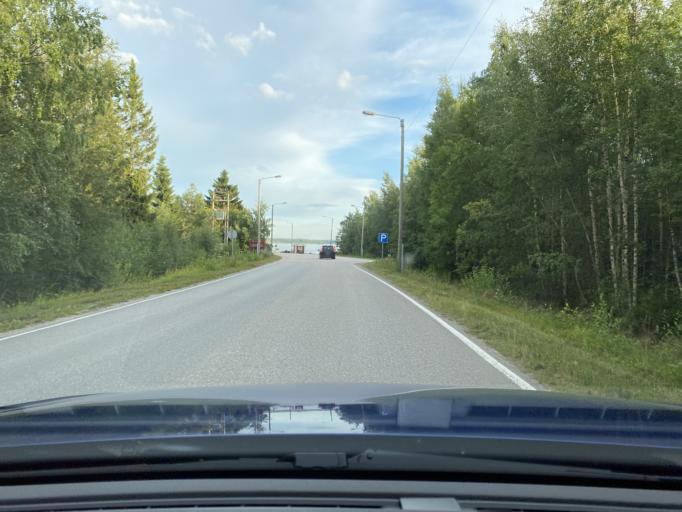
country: FI
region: Ostrobothnia
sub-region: Vaasa
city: Korsnaes
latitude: 62.9455
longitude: 21.1757
